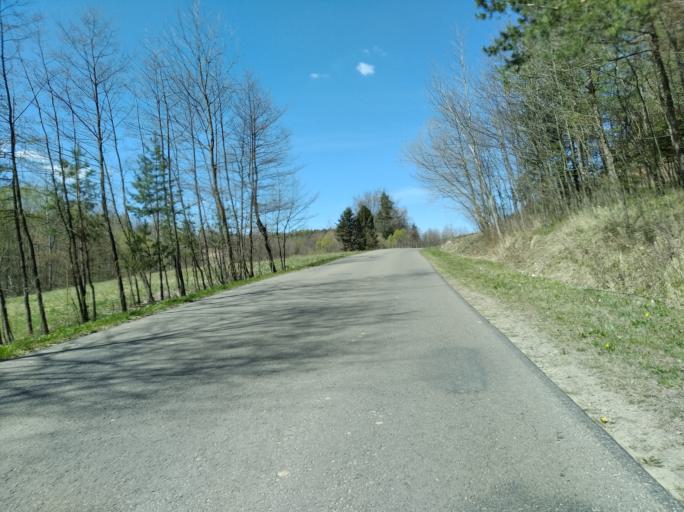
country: PL
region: Subcarpathian Voivodeship
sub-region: Powiat brzozowski
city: Golcowa
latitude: 49.7428
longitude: 22.0786
